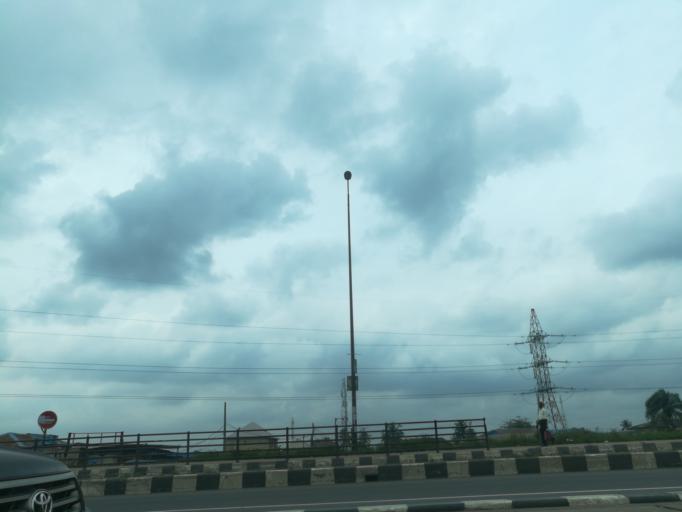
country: NG
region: Lagos
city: Ojota
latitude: 6.6037
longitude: 3.4044
